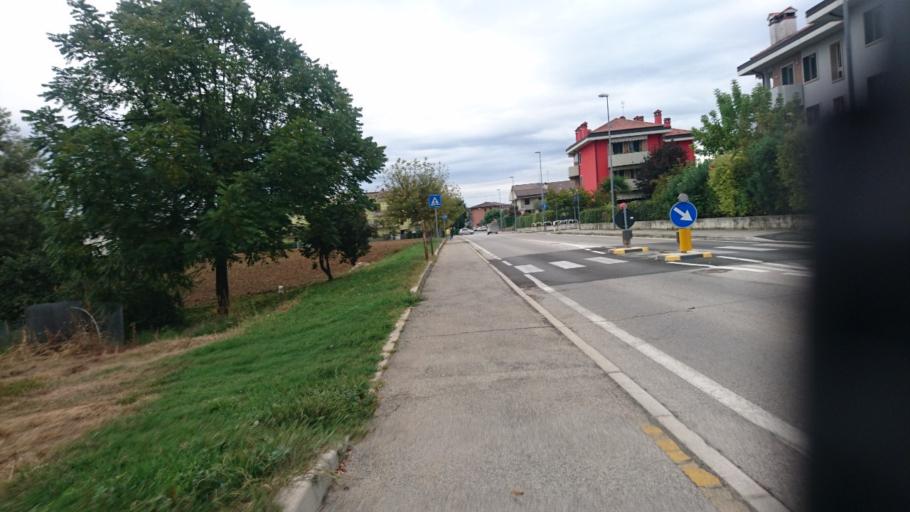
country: IT
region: Veneto
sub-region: Provincia di Vicenza
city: Creazzo
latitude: 45.5338
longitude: 11.4868
